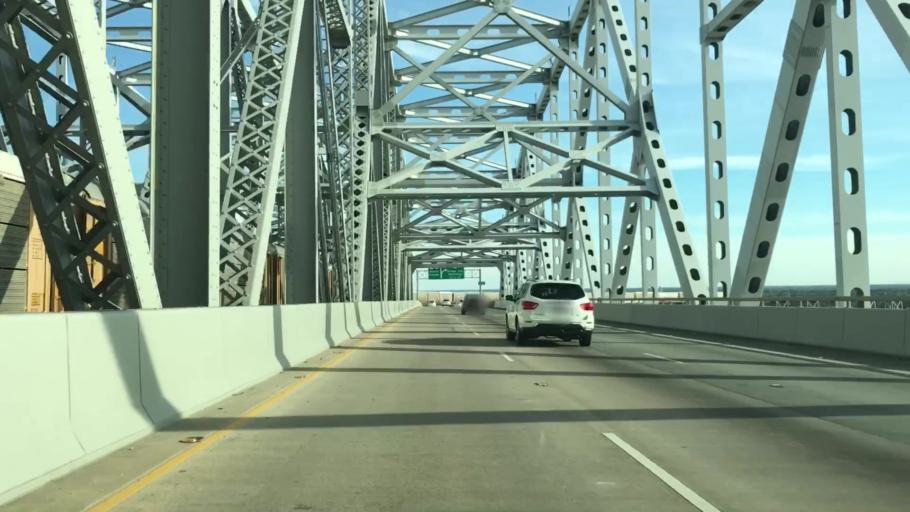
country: US
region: Louisiana
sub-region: Jefferson Parish
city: Bridge City
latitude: 29.9421
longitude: -90.1668
